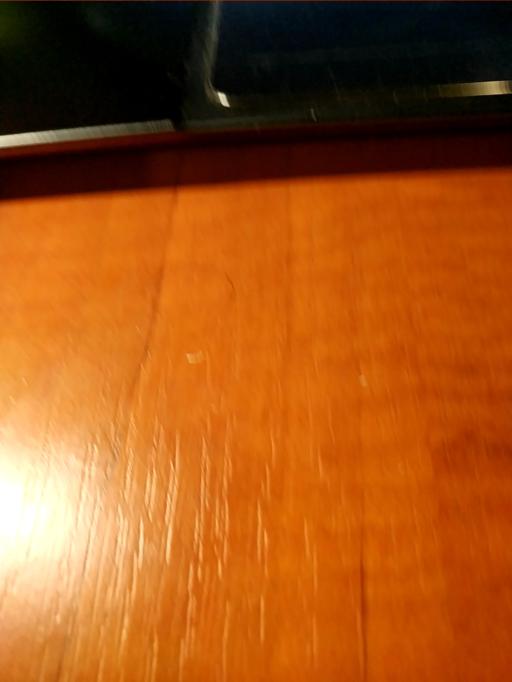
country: RU
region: Kaluga
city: Iznoski
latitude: 54.8587
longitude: 35.3389
